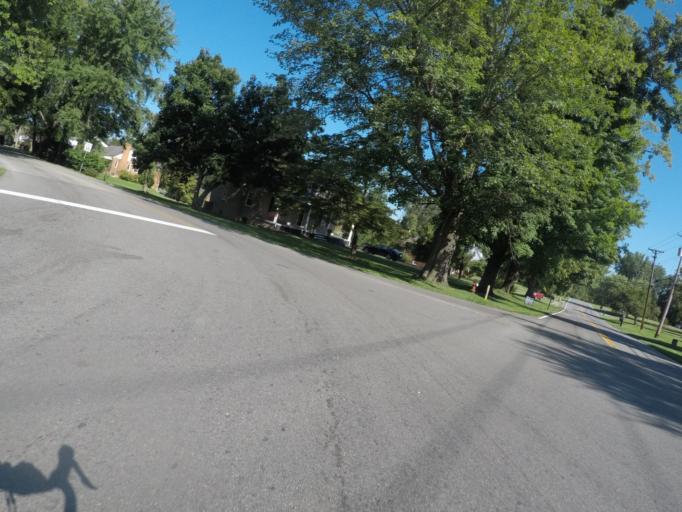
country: US
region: Kentucky
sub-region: Boyd County
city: Westwood
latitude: 38.4897
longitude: -82.6892
